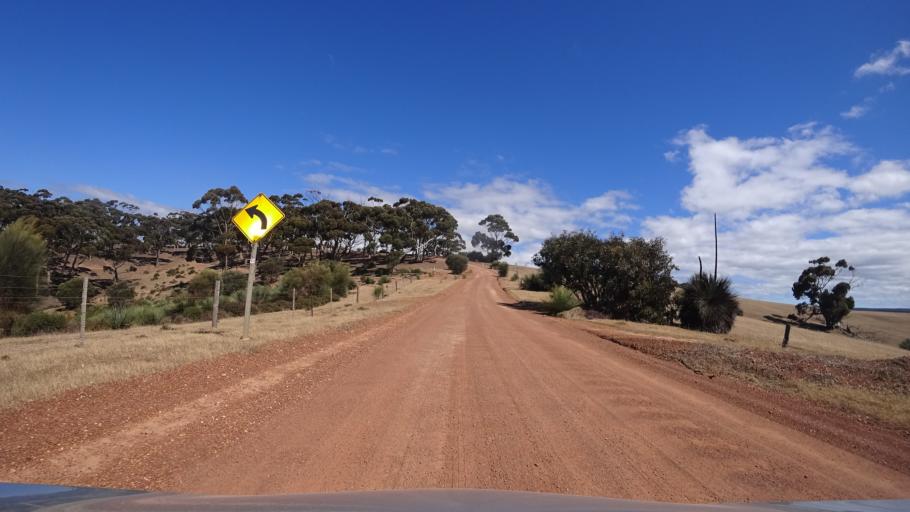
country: AU
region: South Australia
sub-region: Kangaroo Island
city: Kingscote
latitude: -35.6899
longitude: 136.9813
